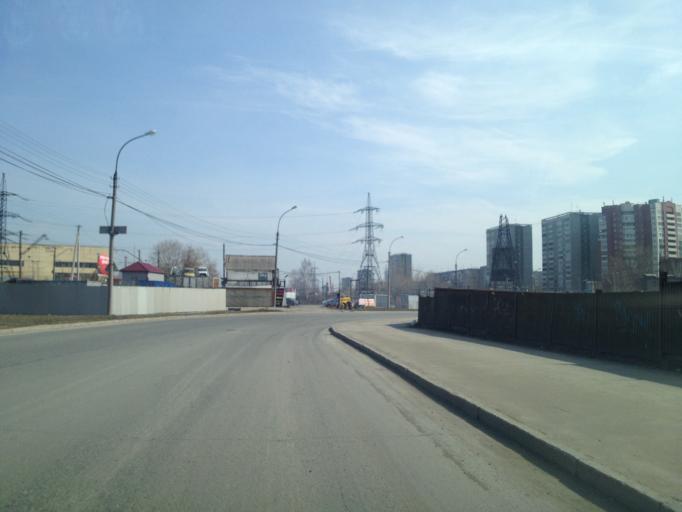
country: RU
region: Sverdlovsk
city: Yekaterinburg
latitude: 56.8780
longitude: 60.5525
